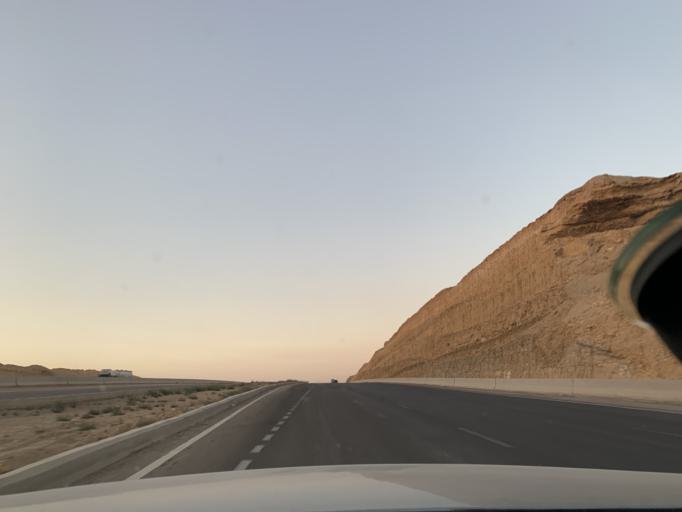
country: EG
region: Muhafazat al Qahirah
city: Halwan
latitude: 29.9498
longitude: 31.5381
